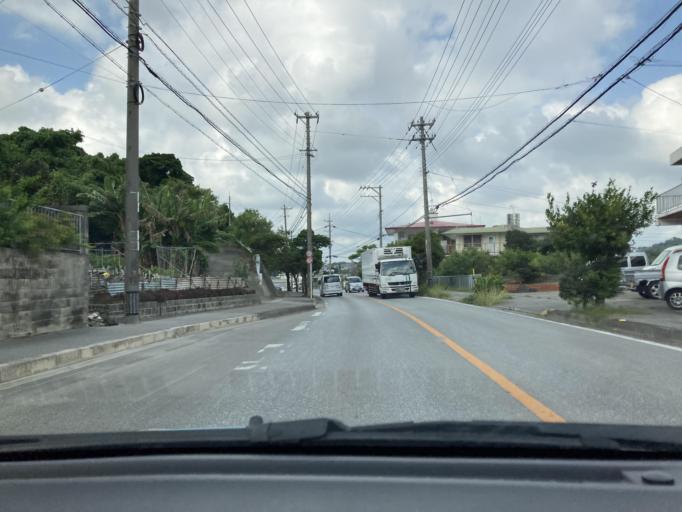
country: JP
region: Okinawa
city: Ginowan
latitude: 26.2811
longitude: 127.7847
